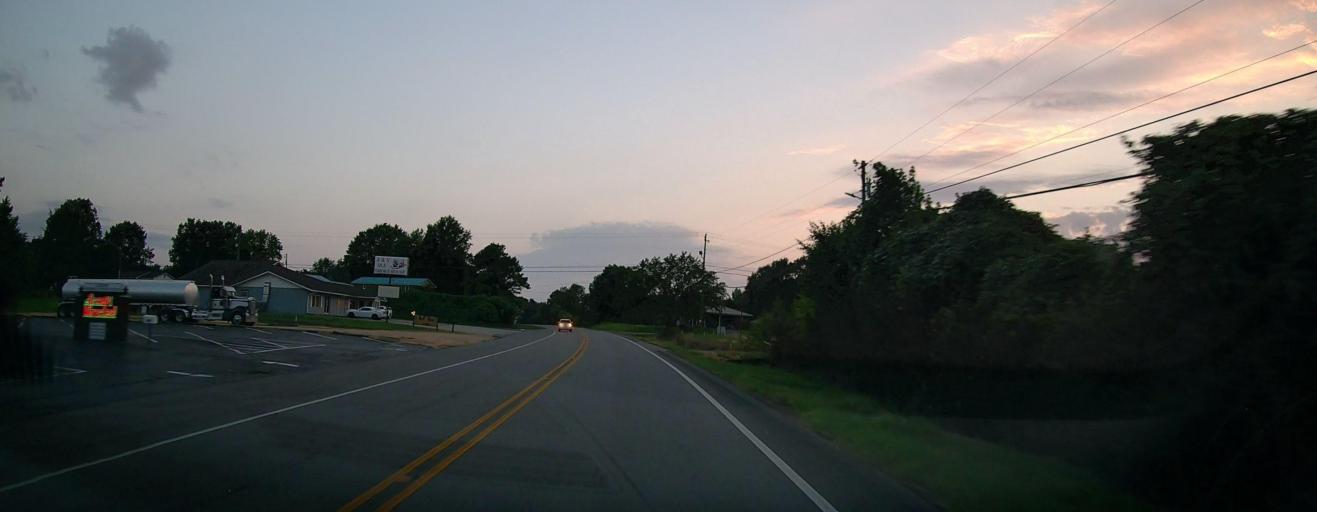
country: US
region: Alabama
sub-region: Marion County
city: Hamilton
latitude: 34.1366
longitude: -88.0170
